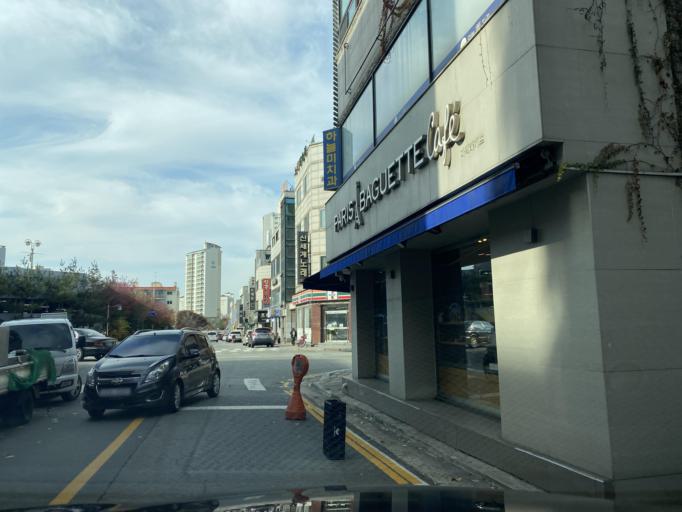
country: KR
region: Chungcheongnam-do
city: Cheonan
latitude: 36.8210
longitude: 127.1585
